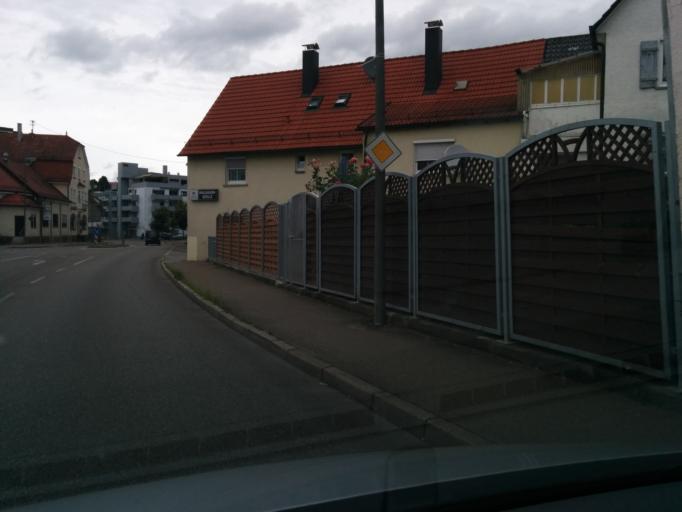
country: DE
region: Baden-Wuerttemberg
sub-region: Regierungsbezirk Stuttgart
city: Wernau
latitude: 48.6873
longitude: 9.4247
